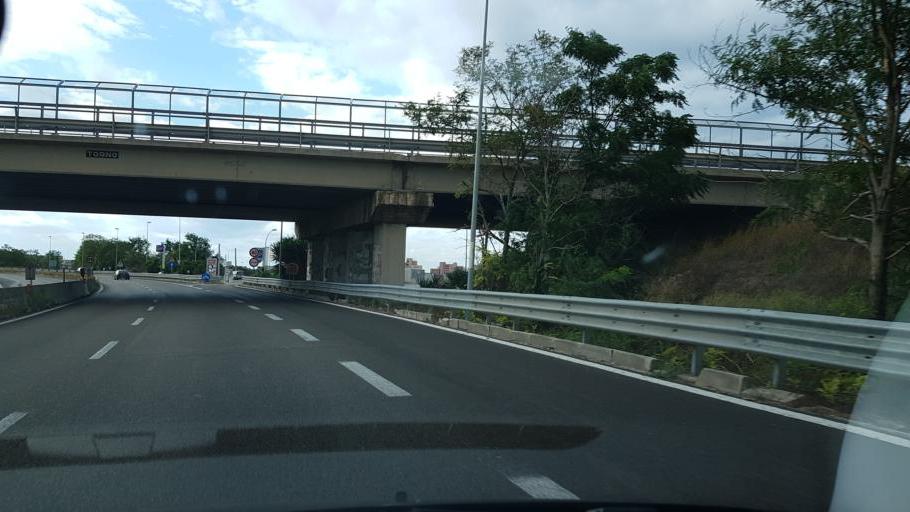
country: IT
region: Apulia
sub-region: Provincia di Brindisi
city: La Rosa
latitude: 40.6165
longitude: 17.9565
